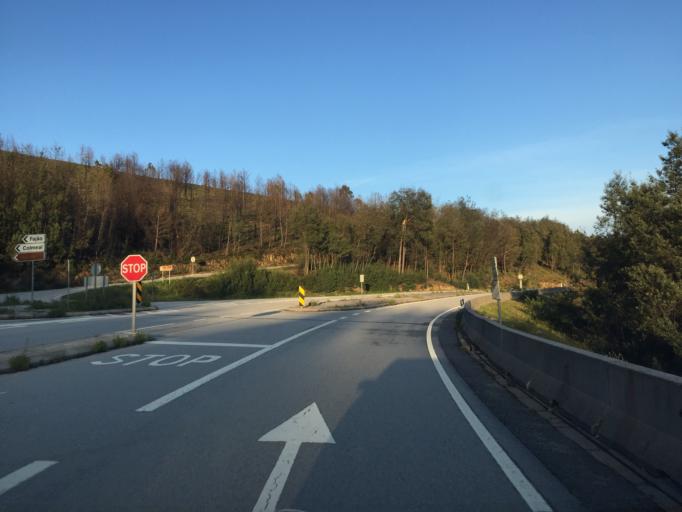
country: PT
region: Coimbra
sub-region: Pampilhosa da Serra
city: Pampilhosa da Serra
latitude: 40.1105
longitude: -8.0164
